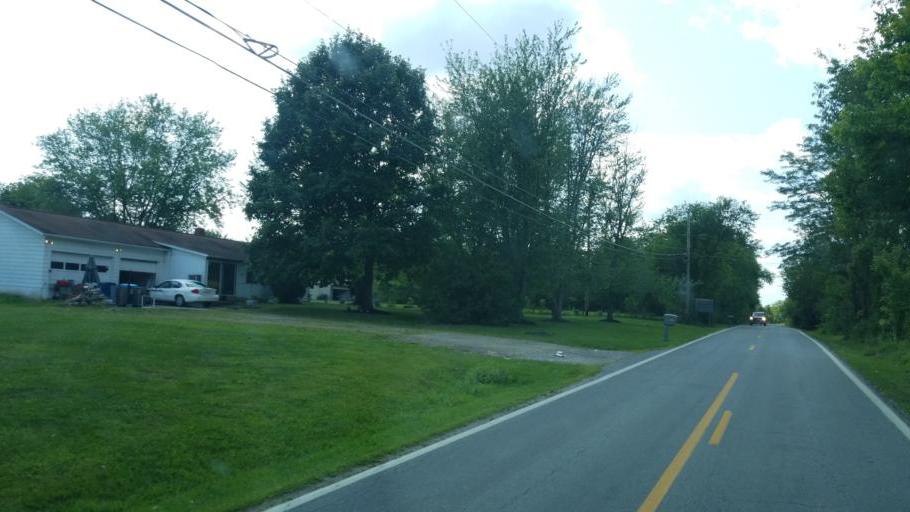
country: US
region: Ohio
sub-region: Delaware County
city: Lewis Center
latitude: 40.2256
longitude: -82.9828
